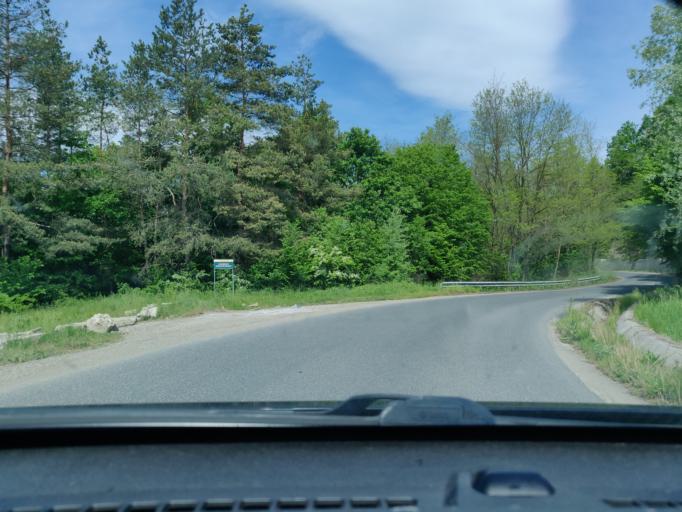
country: RO
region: Vrancea
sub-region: Comuna Vidra
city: Vidra
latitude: 45.9321
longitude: 26.8892
